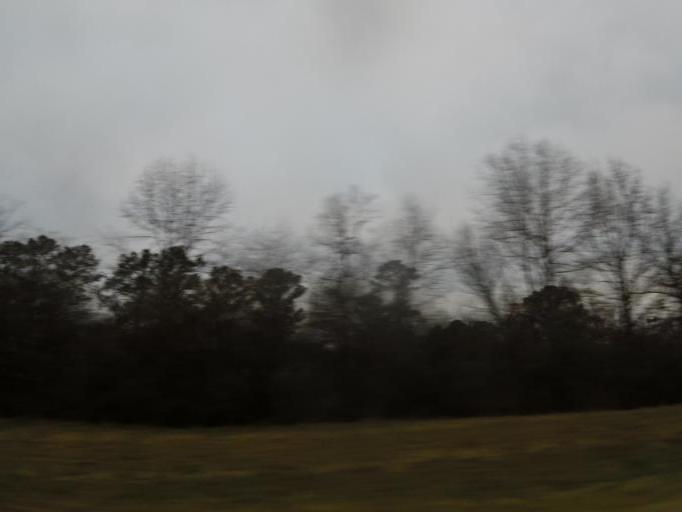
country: US
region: Alabama
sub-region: Blount County
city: Smoke Rise
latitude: 33.9630
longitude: -86.8674
